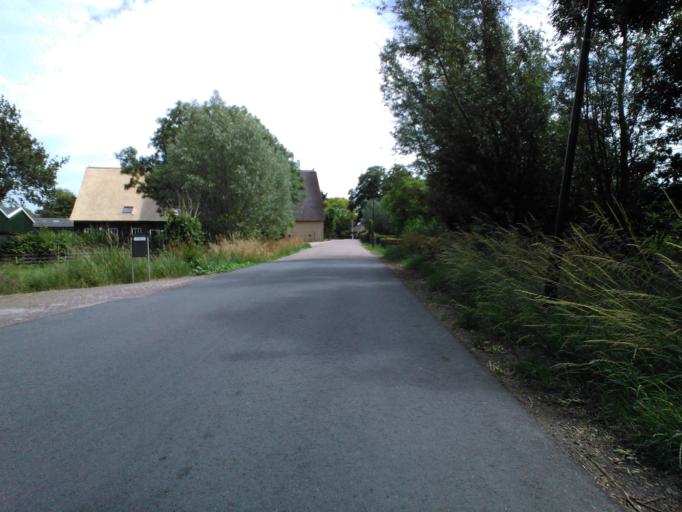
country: NL
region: South Holland
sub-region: Gemeente Hardinxveld-Giessendam
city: Neder-Hardinxveld
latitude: 51.8442
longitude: 4.8693
